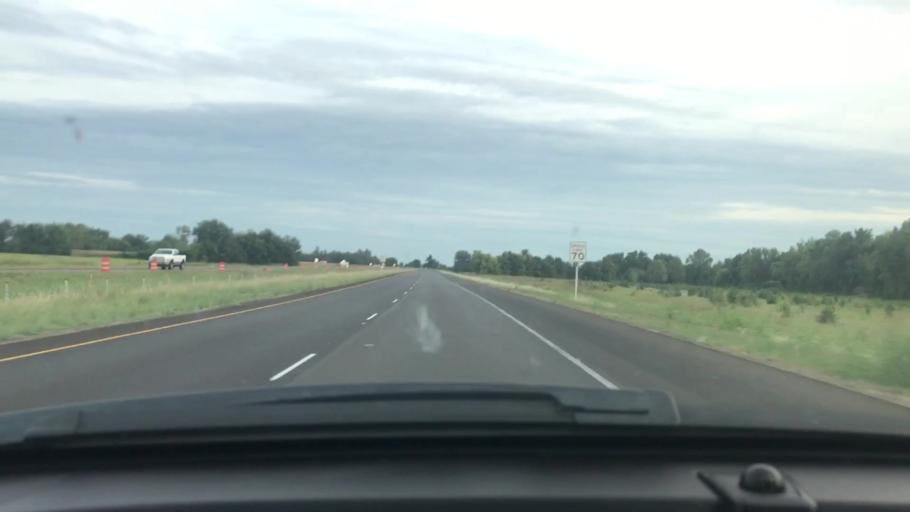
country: US
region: Arkansas
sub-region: Poinsett County
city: Trumann
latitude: 35.6699
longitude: -90.5527
